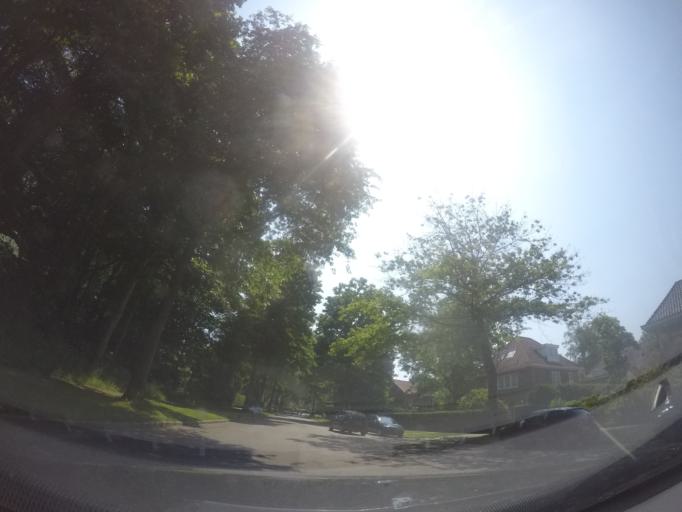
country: NL
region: Gelderland
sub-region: Gemeente Rheden
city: Velp
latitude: 52.0033
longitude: 5.9821
